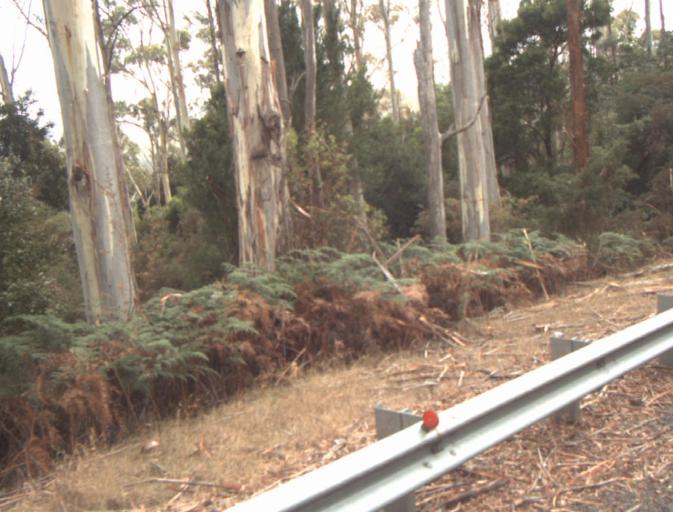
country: AU
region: Tasmania
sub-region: Dorset
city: Bridport
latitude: -41.1669
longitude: 147.2327
